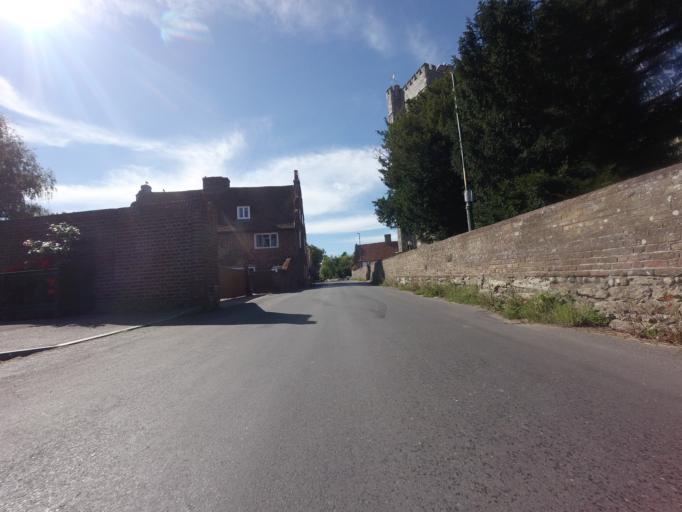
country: GB
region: England
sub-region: Kent
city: Birchington-on-Sea
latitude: 51.3539
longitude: 1.2519
